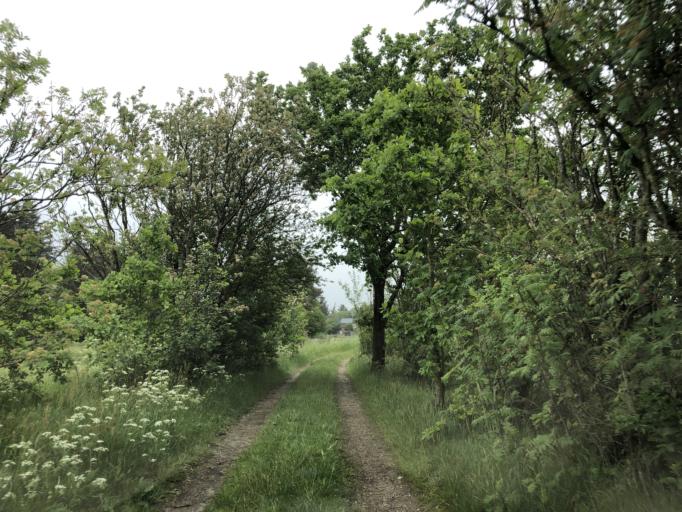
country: DK
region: Central Jutland
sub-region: Holstebro Kommune
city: Holstebro
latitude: 56.3339
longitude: 8.4805
